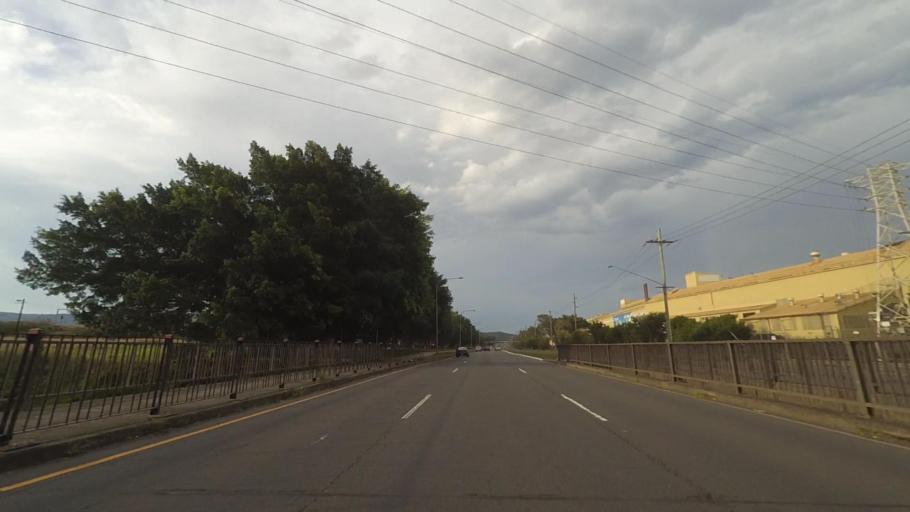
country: AU
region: New South Wales
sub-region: Wollongong
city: Cringila
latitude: -34.4610
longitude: 150.8723
